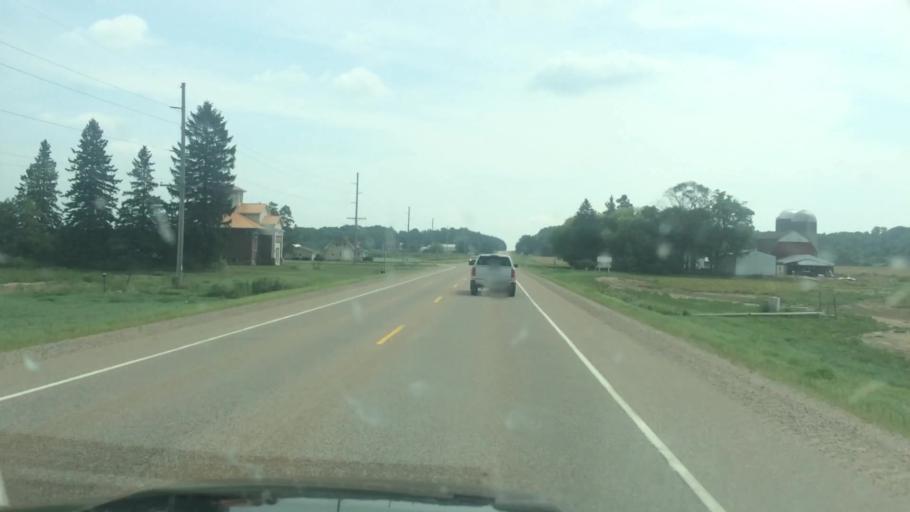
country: US
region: Wisconsin
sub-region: Langlade County
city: Antigo
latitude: 45.1623
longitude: -89.0747
